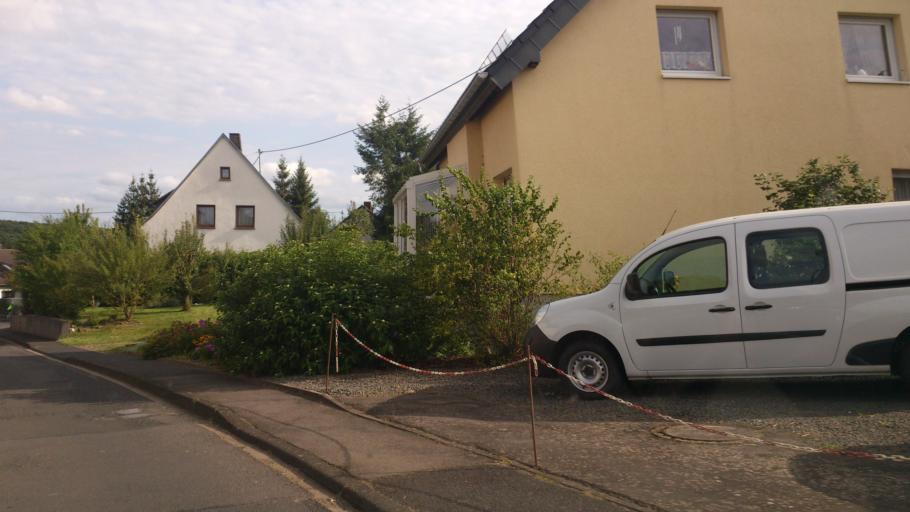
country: DE
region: Rheinland-Pfalz
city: Nohn
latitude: 50.3330
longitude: 6.7868
